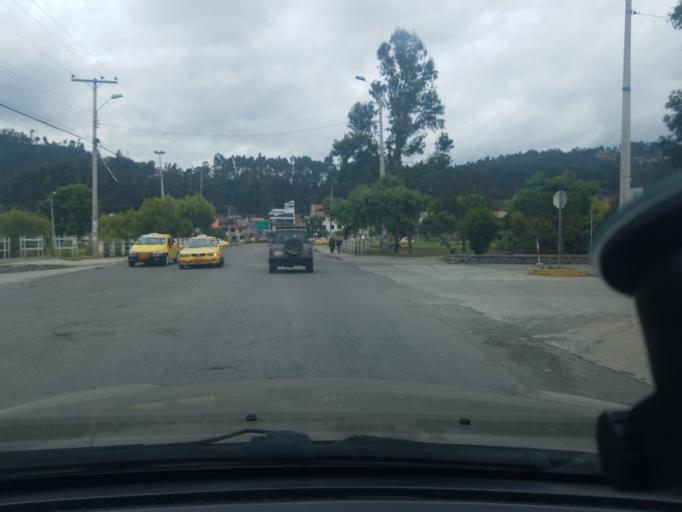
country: EC
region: Azuay
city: Cuenca
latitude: -2.8987
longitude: -78.9756
